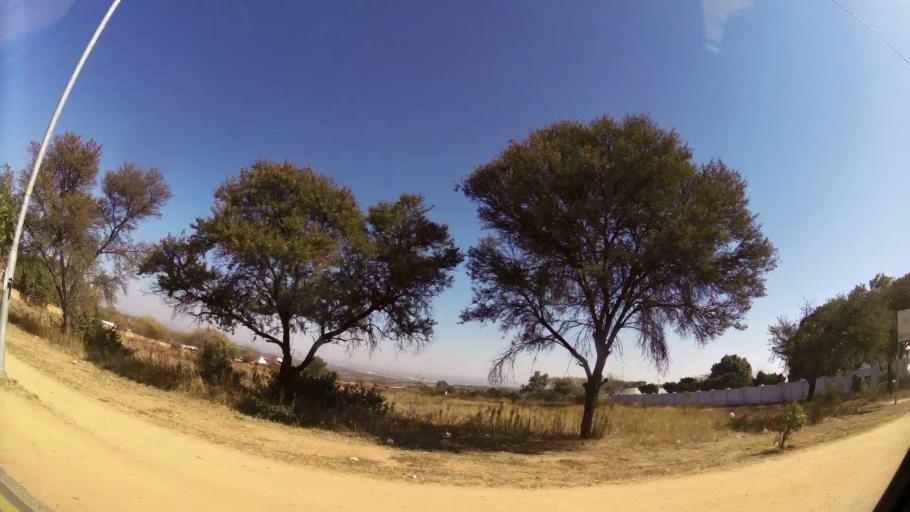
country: ZA
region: Gauteng
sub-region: City of Johannesburg Metropolitan Municipality
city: Midrand
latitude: -25.9430
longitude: 28.0967
